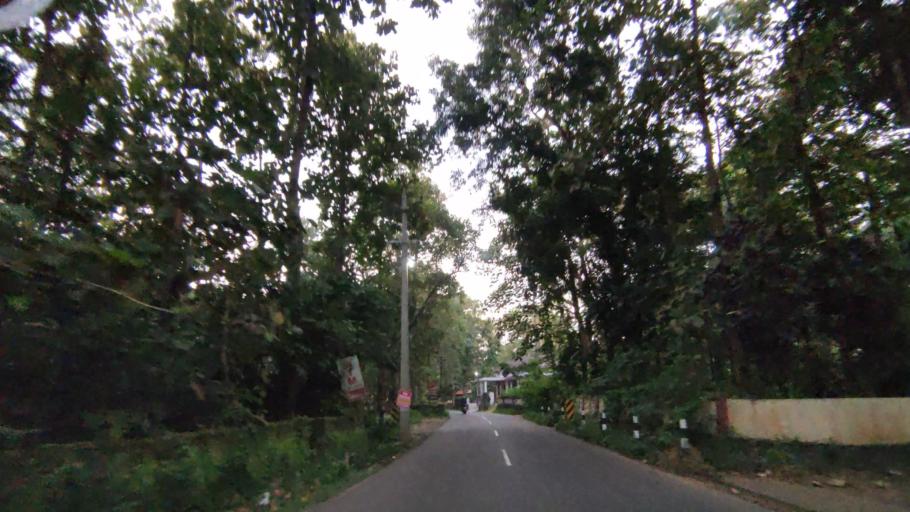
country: IN
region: Kerala
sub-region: Kottayam
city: Kottayam
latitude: 9.6656
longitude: 76.5071
